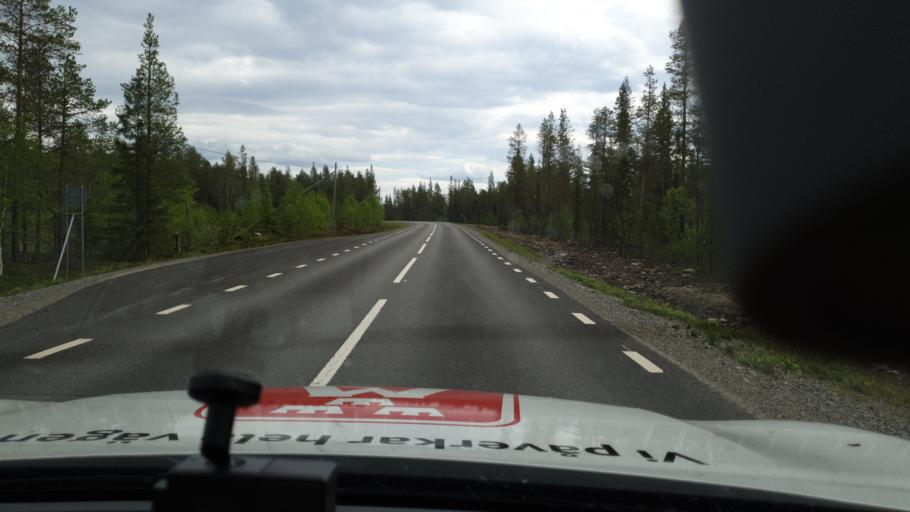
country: SE
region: Vaesterbotten
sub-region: Sorsele Kommun
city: Sorsele
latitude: 65.7662
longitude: 17.0567
